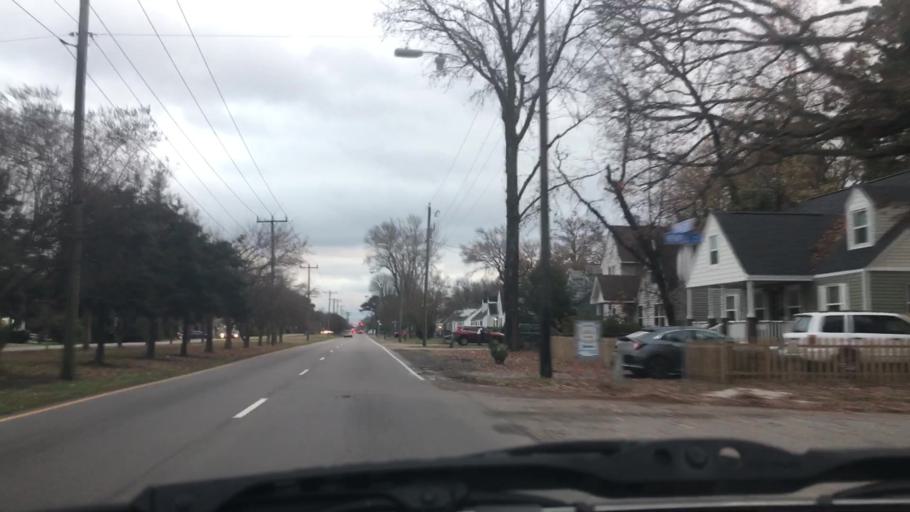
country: US
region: Virginia
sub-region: City of Norfolk
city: Norfolk
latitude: 36.9214
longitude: -76.2427
